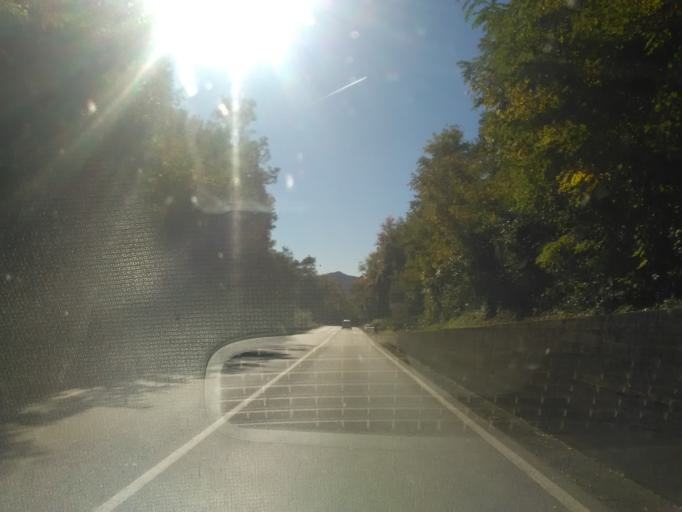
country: IT
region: Piedmont
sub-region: Provincia di Vercelli
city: Quarona
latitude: 45.7578
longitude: 8.2590
